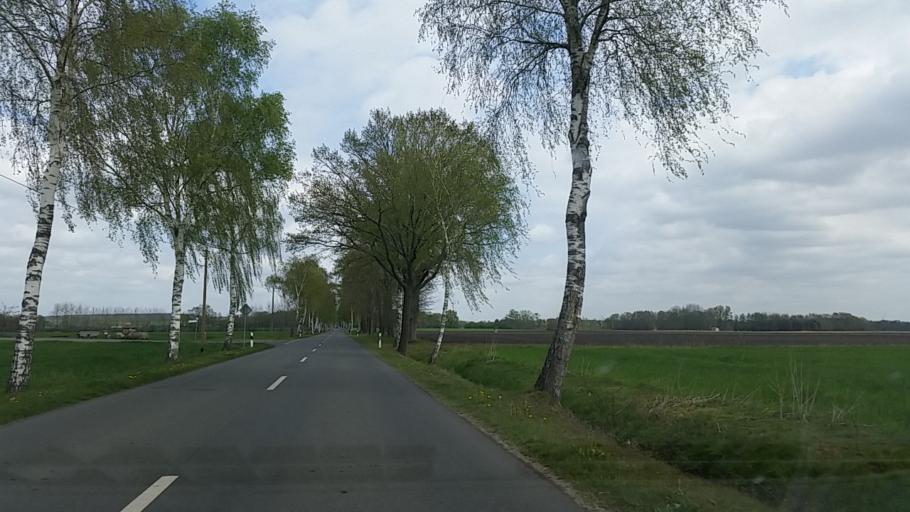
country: DE
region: Lower Saxony
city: Konigsmoor
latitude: 53.2062
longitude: 9.7088
